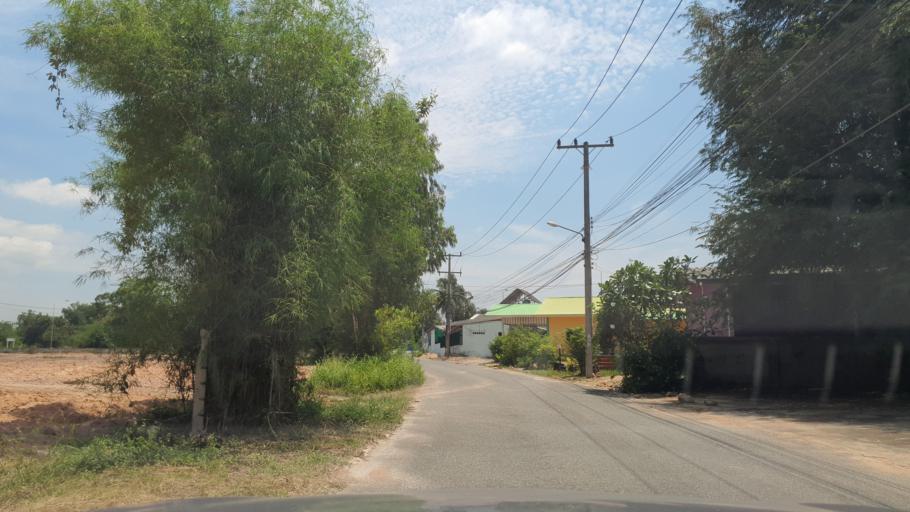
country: TH
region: Rayong
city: Ban Chang
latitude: 12.8001
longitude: 100.9463
